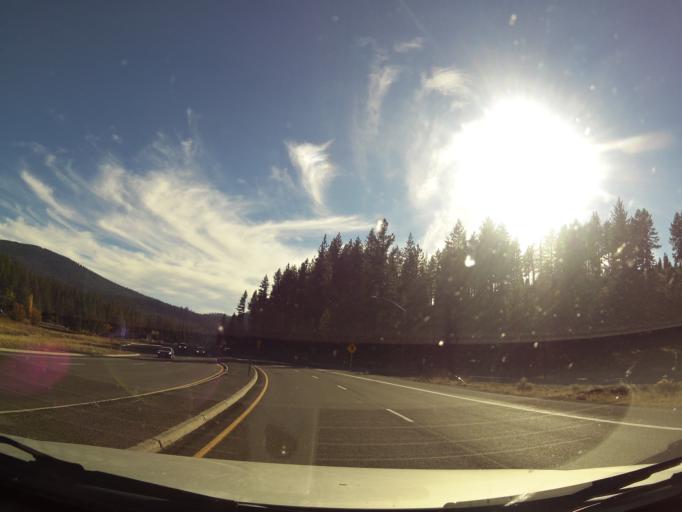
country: US
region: Nevada
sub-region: Douglas County
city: Kingsbury
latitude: 39.1004
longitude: -119.9099
